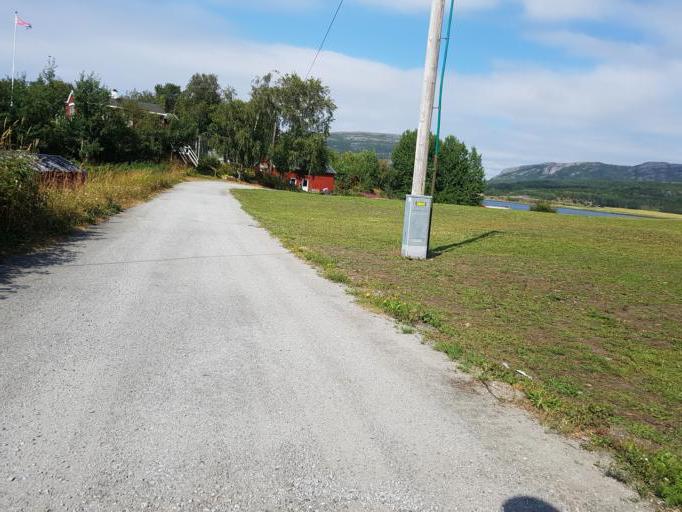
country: NO
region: Sor-Trondelag
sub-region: Agdenes
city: Lensvik
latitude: 63.6358
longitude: 9.8384
